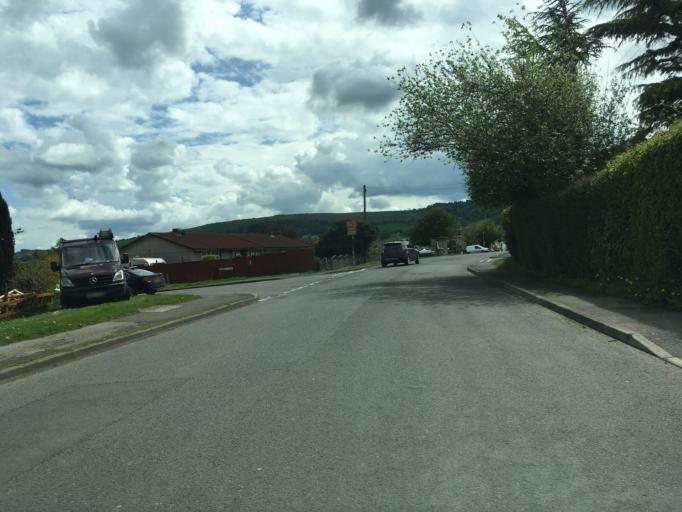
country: GB
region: England
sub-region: Gloucestershire
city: Stonehouse
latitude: 51.7321
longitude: -2.2810
